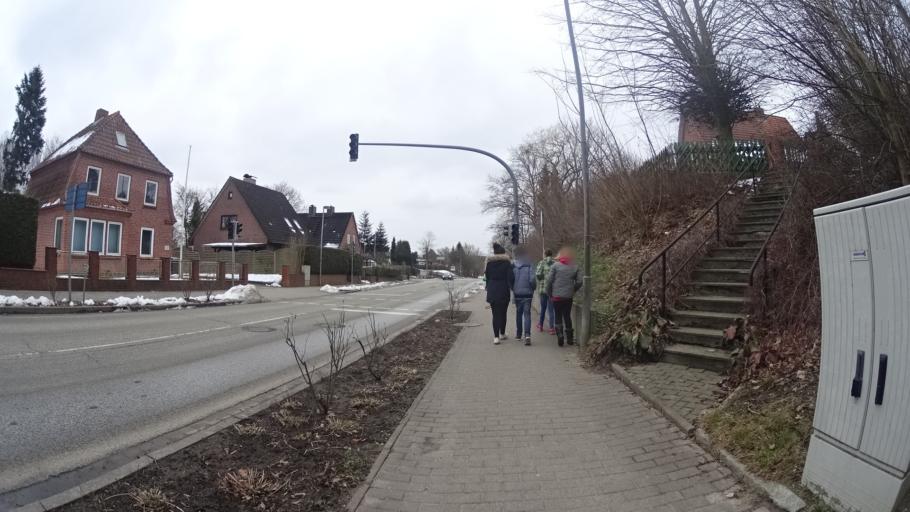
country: DE
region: Schleswig-Holstein
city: Lutjenburg
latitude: 54.2880
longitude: 10.5833
